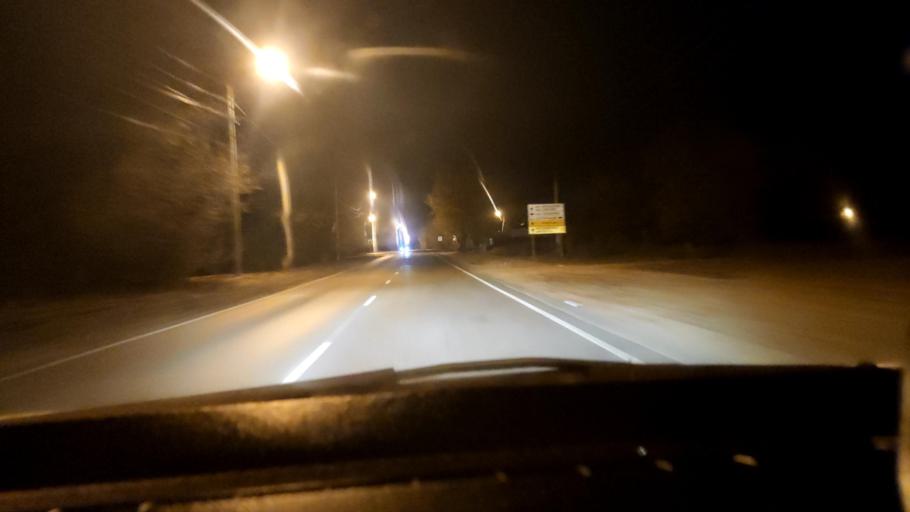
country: RU
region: Voronezj
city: Pridonskoy
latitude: 51.6430
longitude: 39.0940
